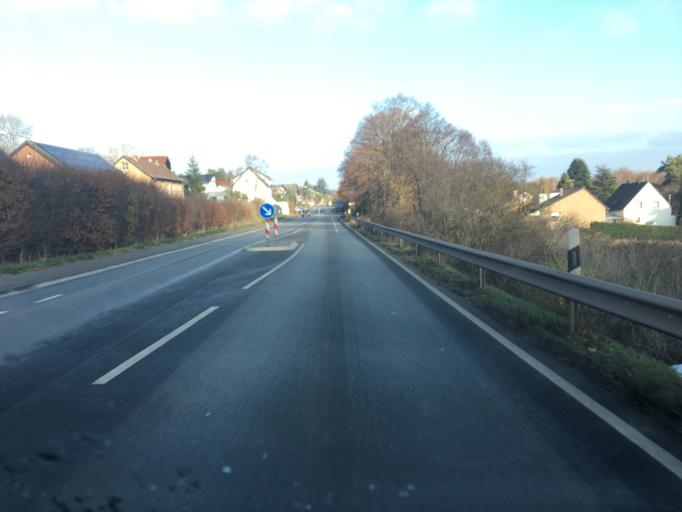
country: DE
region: North Rhine-Westphalia
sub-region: Regierungsbezirk Koln
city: Mechernich
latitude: 50.5826
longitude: 6.6071
